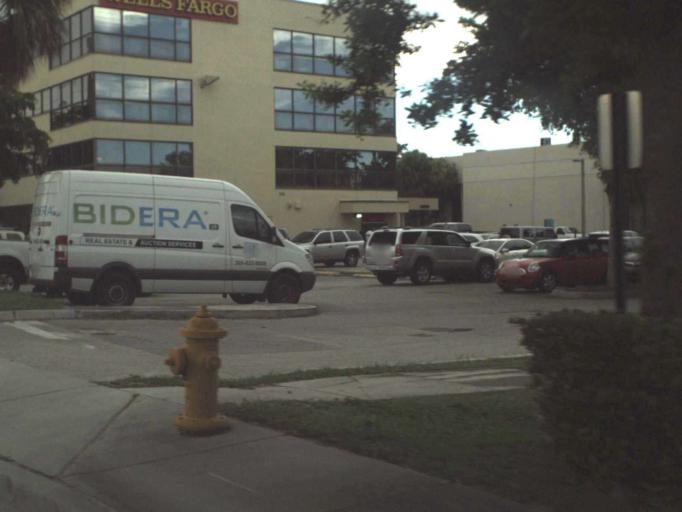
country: US
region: Florida
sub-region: Miami-Dade County
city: Virginia Gardens
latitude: 25.8178
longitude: -80.3134
